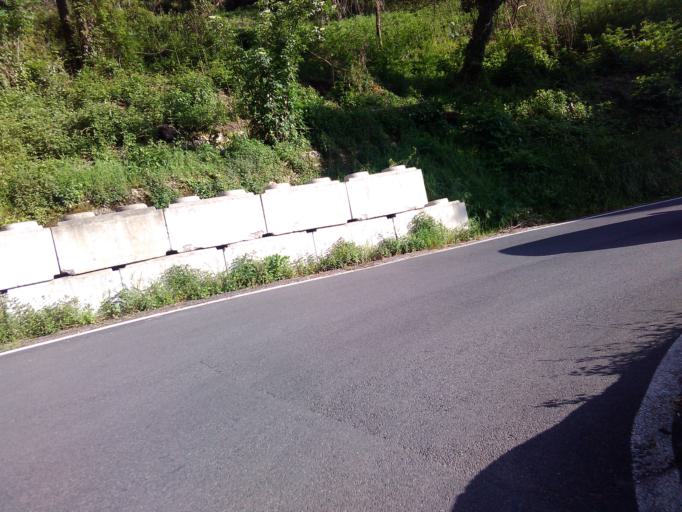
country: IT
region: Tuscany
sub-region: Provincia di Lucca
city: Piano di Mommio
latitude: 43.9418
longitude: 10.2634
